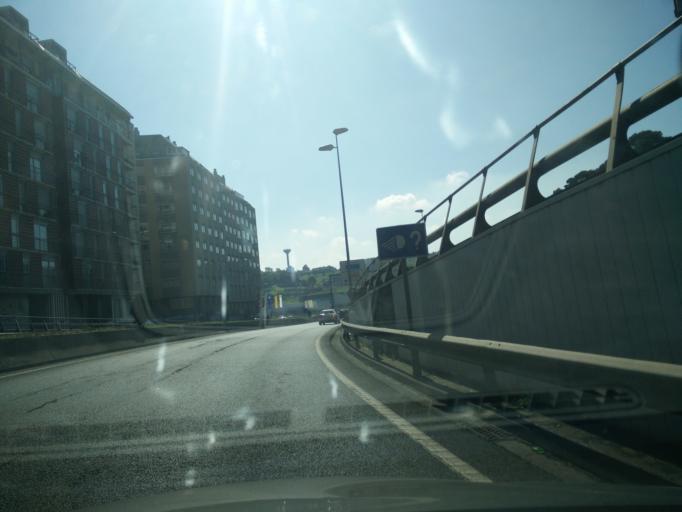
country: ES
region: Galicia
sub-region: Provincia da Coruna
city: A Coruna
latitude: 43.3510
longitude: -8.3903
